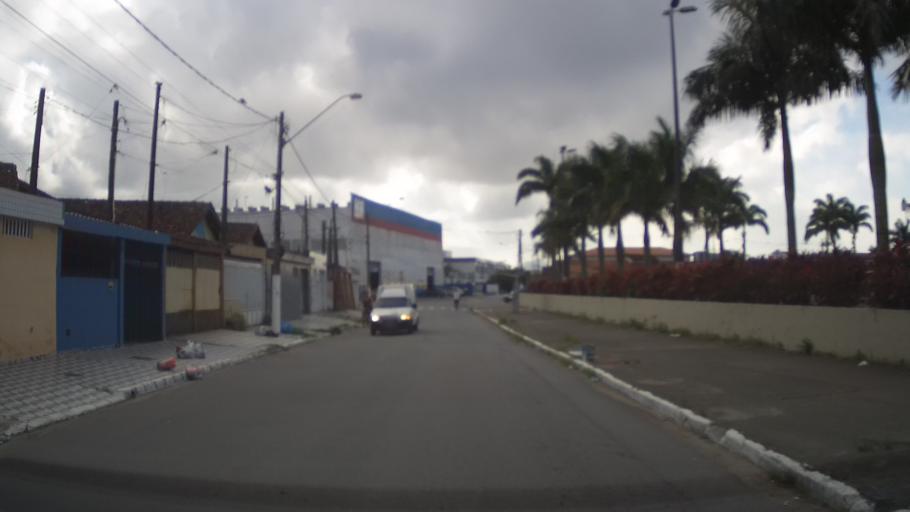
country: BR
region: Sao Paulo
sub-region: Praia Grande
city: Praia Grande
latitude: -24.0178
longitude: -46.4750
